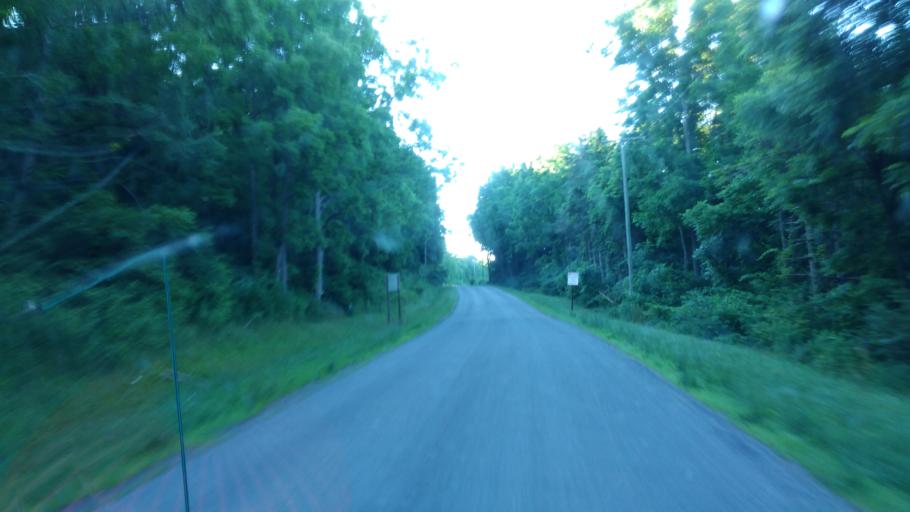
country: US
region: New York
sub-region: Wayne County
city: Lyons
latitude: 43.1146
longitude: -77.0359
